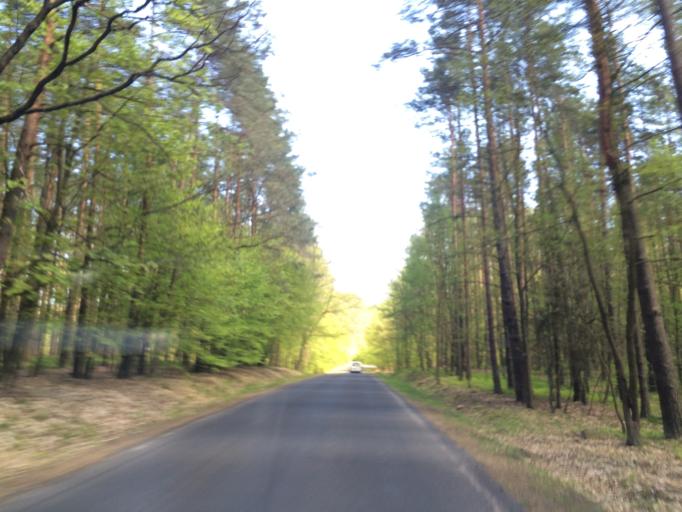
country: PL
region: Warmian-Masurian Voivodeship
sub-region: Powiat nowomiejski
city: Biskupiec
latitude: 53.3850
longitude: 19.3853
